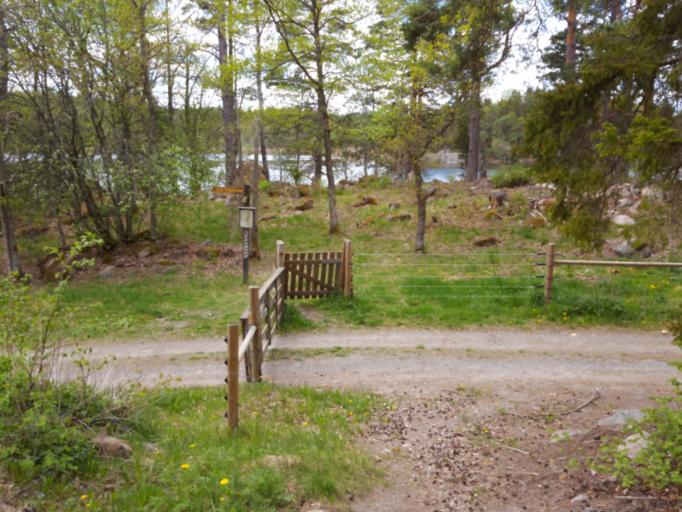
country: SE
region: Uppsala
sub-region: Knivsta Kommun
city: Knivsta
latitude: 59.8375
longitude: 17.9011
